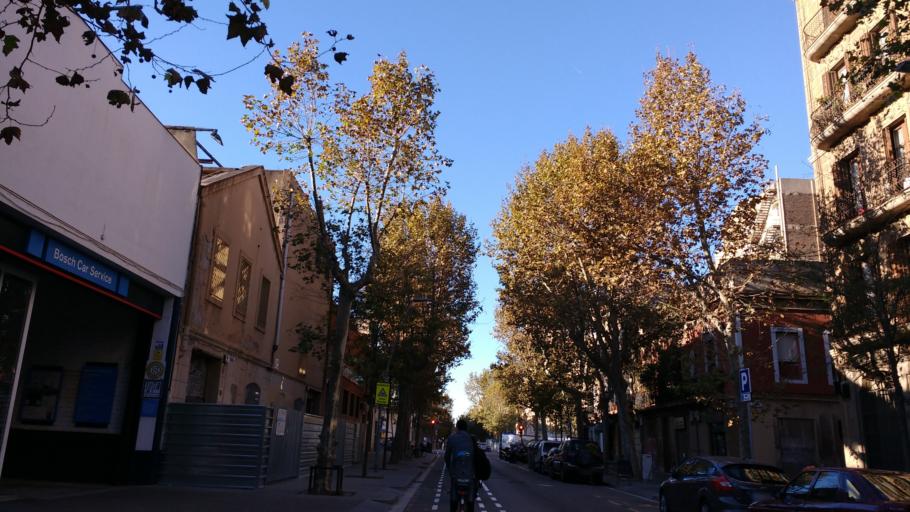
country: ES
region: Catalonia
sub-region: Provincia de Barcelona
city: Sant Marti
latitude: 41.3980
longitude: 2.2004
